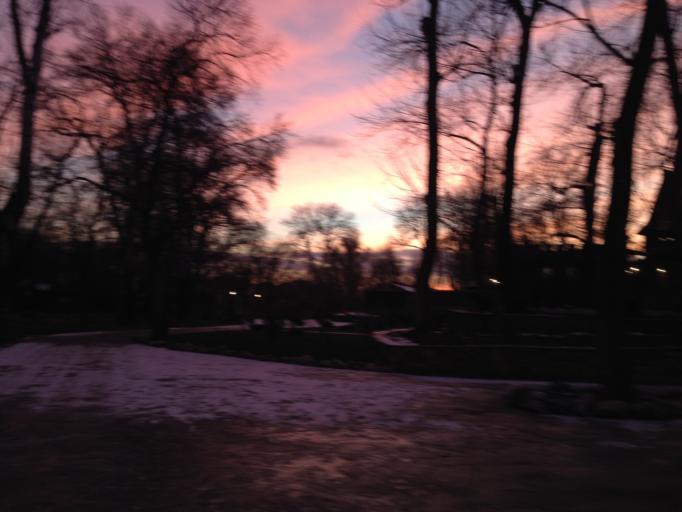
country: RU
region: Rostov
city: Staraya Stanitsa
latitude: 48.3525
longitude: 40.2963
